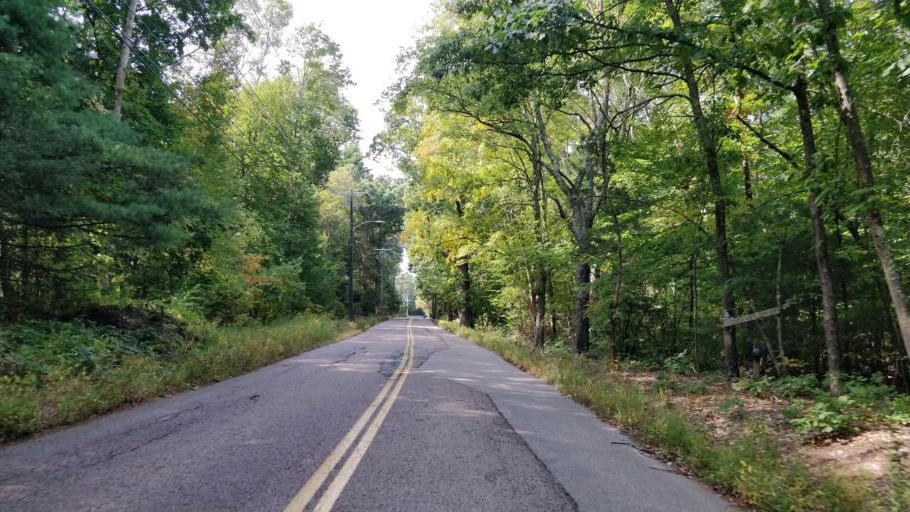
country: US
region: Massachusetts
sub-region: Bristol County
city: Attleboro
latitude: 41.9407
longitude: -71.2416
